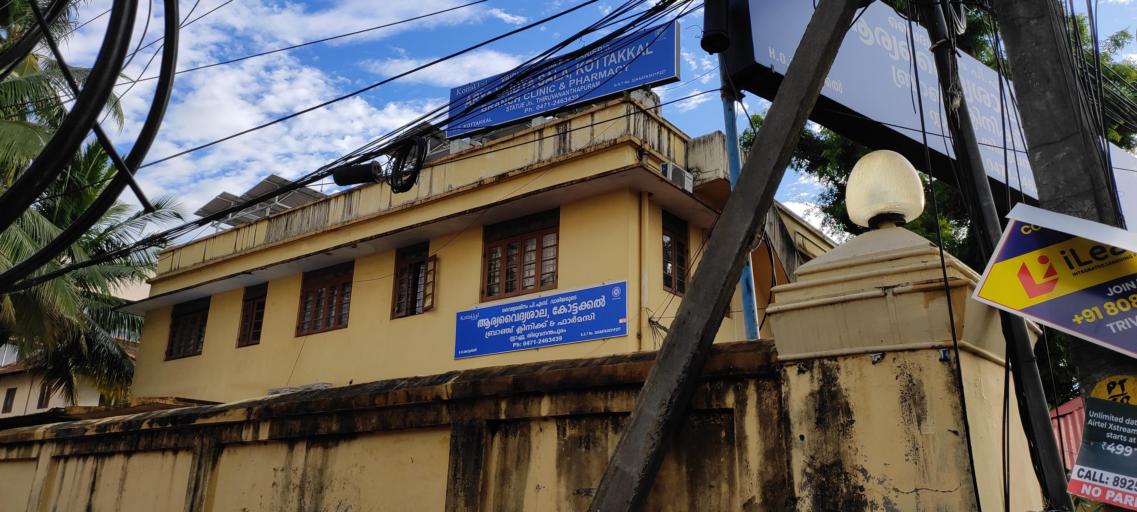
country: IN
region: Kerala
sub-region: Thiruvananthapuram
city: Thiruvananthapuram
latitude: 8.4979
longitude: 76.9480
